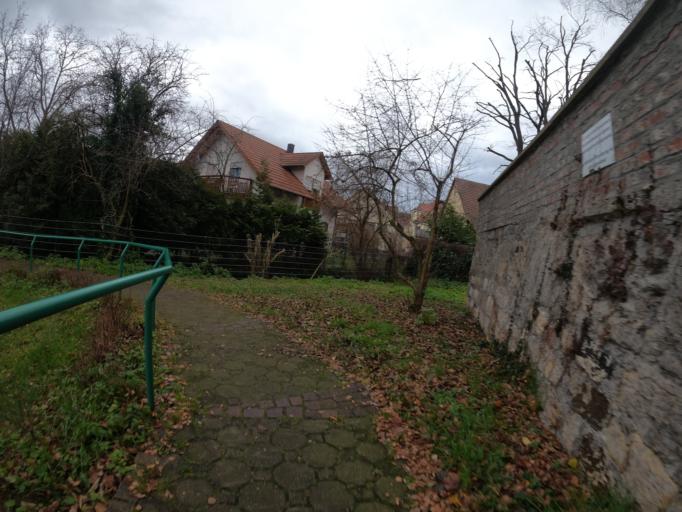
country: DE
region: Baden-Wuerttemberg
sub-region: Regierungsbezirk Stuttgart
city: Sussen
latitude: 48.6792
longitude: 9.7566
